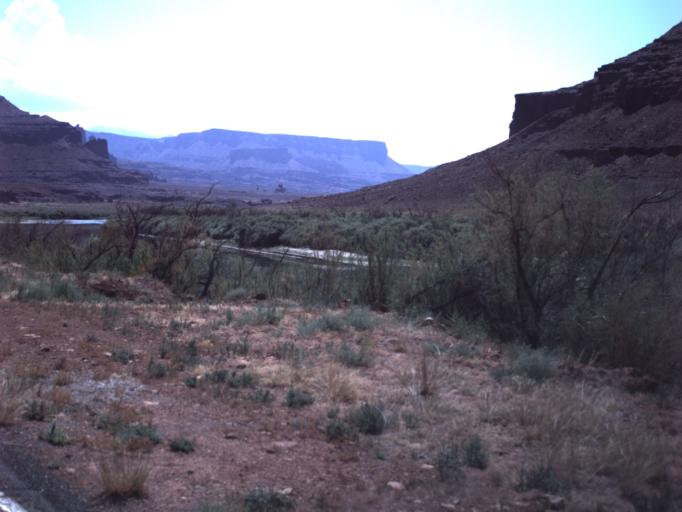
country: US
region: Utah
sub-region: Grand County
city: Moab
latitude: 38.7737
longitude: -109.3258
